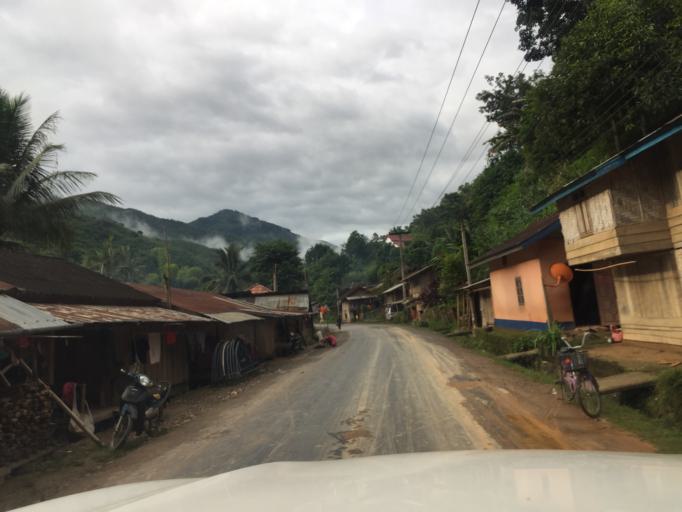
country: LA
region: Oudomxai
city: Muang La
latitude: 21.0554
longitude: 102.2403
